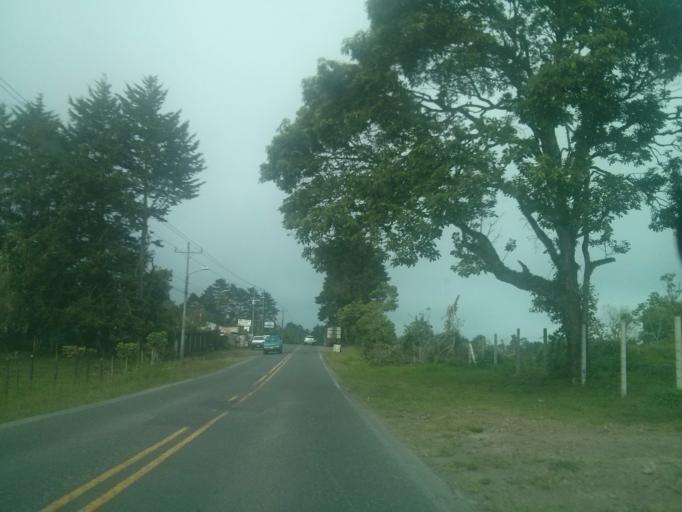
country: CR
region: Cartago
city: Cot
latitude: 9.8789
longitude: -83.8200
